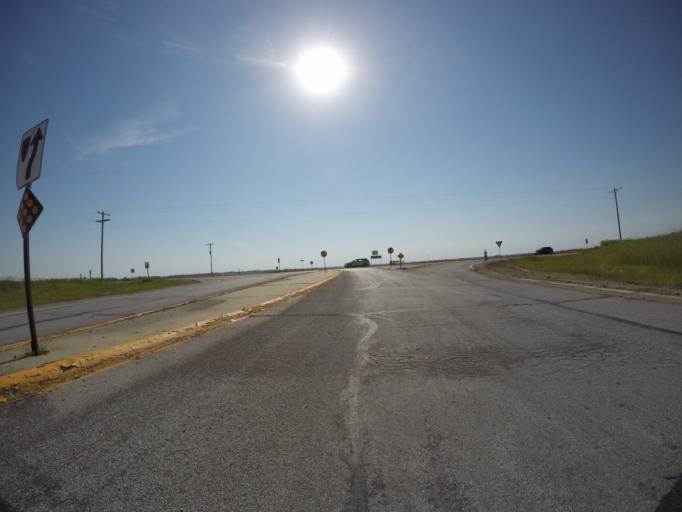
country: US
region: Nebraska
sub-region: Pawnee County
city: Pawnee City
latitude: 40.0446
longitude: -96.3508
